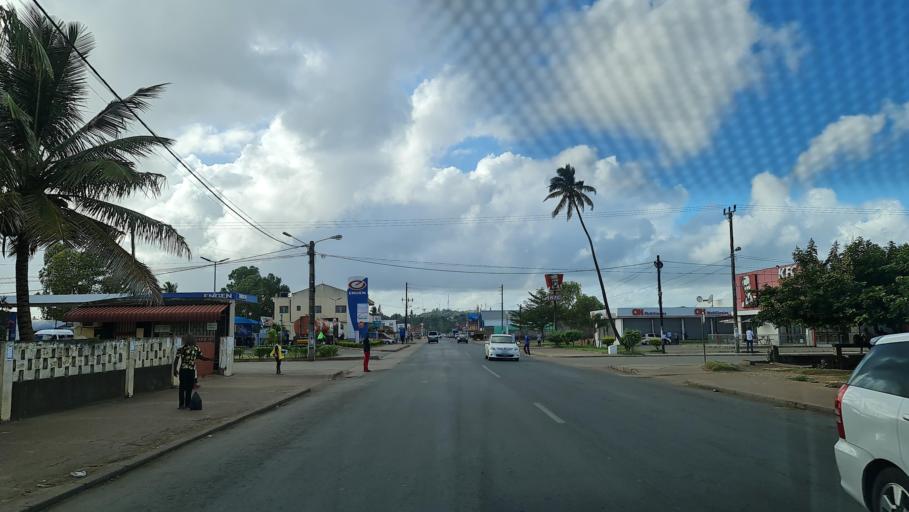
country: MZ
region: Gaza
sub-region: Xai-Xai District
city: Xai-Xai
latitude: -25.0474
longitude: 33.6450
